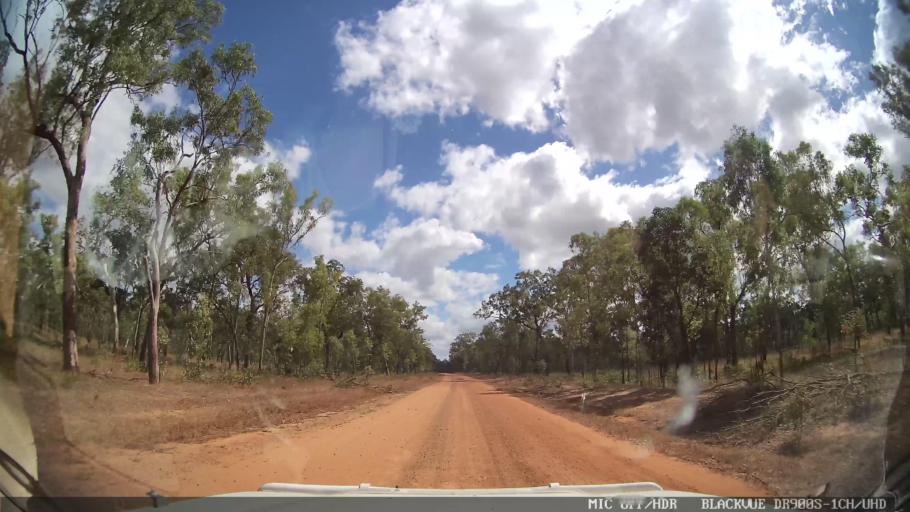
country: AU
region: Queensland
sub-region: Cook
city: Cooktown
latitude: -15.3517
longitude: 144.4646
